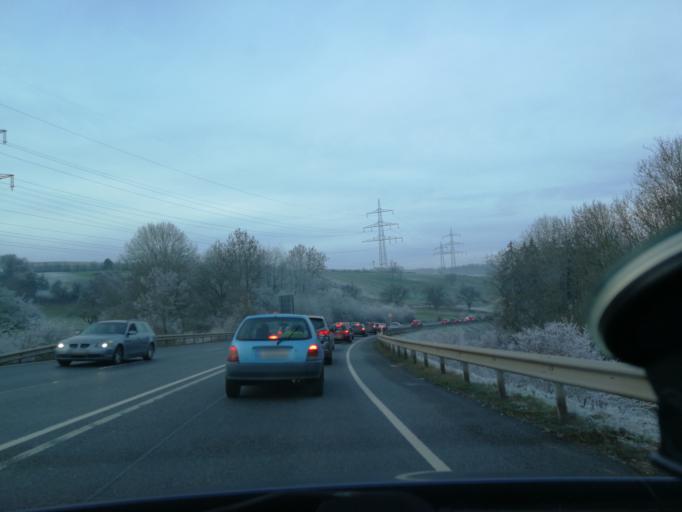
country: DE
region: Rheinland-Pfalz
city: Aach
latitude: 49.7835
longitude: 6.5748
